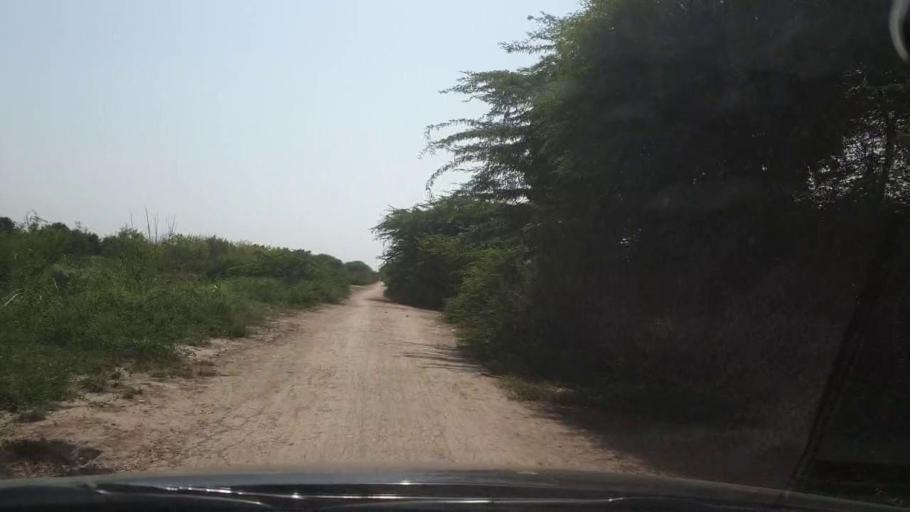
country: PK
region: Sindh
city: Naukot
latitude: 24.8045
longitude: 69.2560
